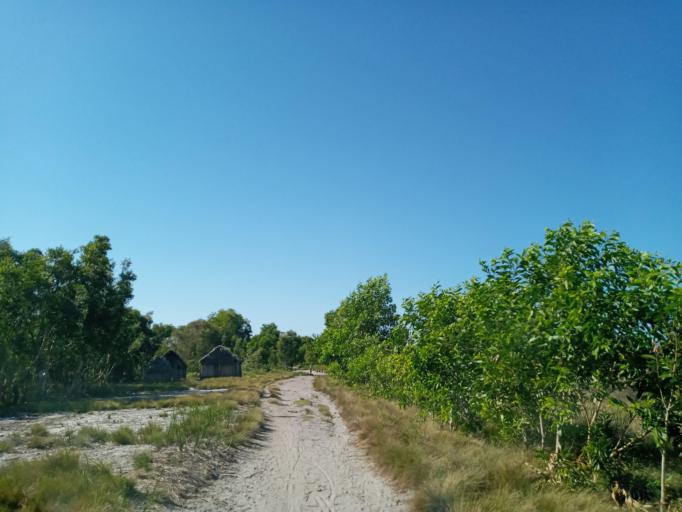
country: MG
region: Anosy
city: Fort Dauphin
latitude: -24.9068
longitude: 47.0966
